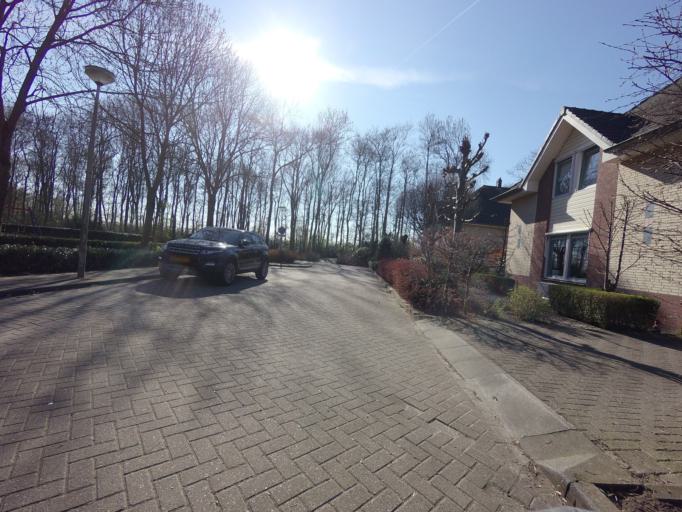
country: NL
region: South Holland
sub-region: Gemeente Vlist
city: Haastrecht
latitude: 51.9984
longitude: 4.7740
